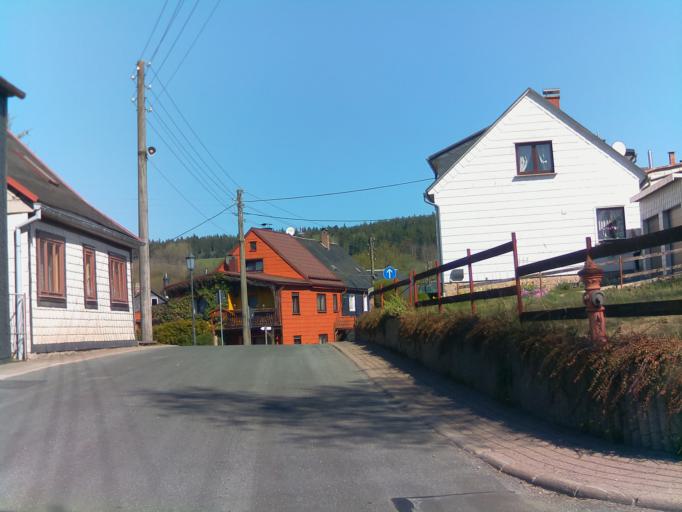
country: DE
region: Thuringia
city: Gillersdorf
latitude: 50.6030
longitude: 11.0209
